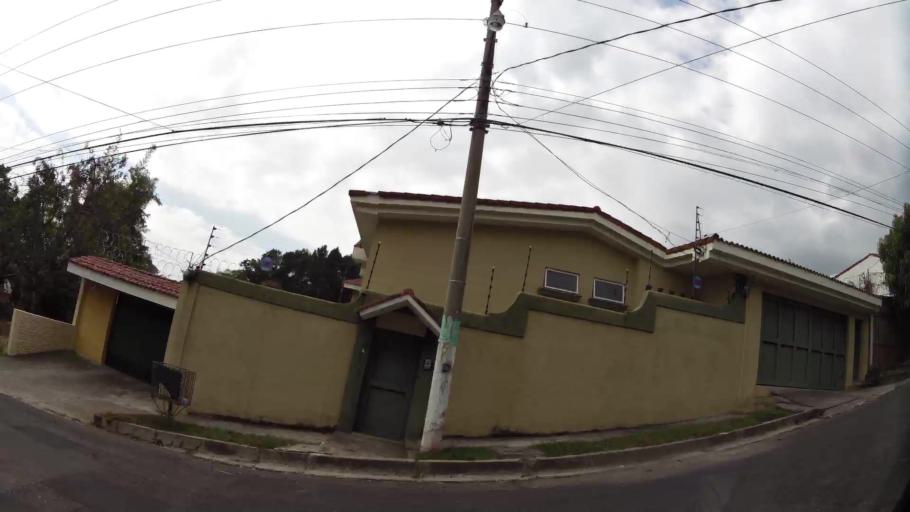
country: SV
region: La Libertad
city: Santa Tecla
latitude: 13.7106
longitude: -89.2559
